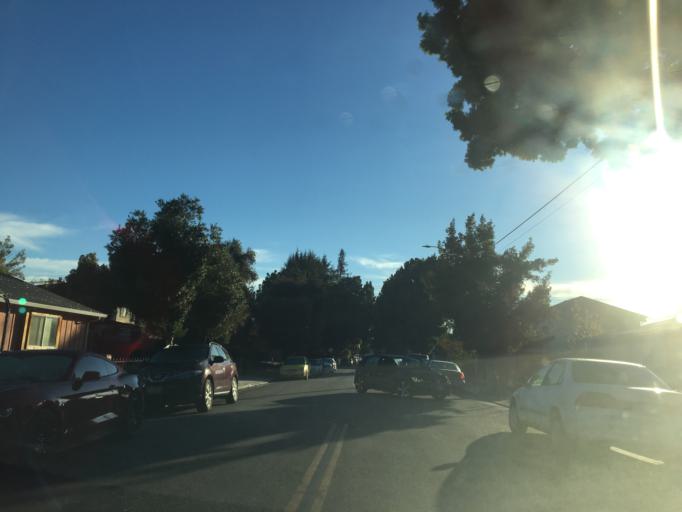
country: US
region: California
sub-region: Santa Clara County
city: Sunnyvale
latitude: 37.3843
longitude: -122.0220
